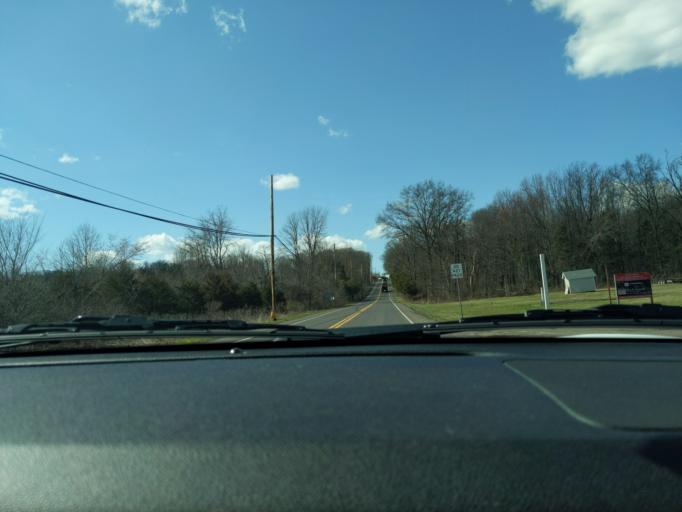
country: US
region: Pennsylvania
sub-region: Bucks County
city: Perkasie
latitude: 40.4040
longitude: -75.2545
